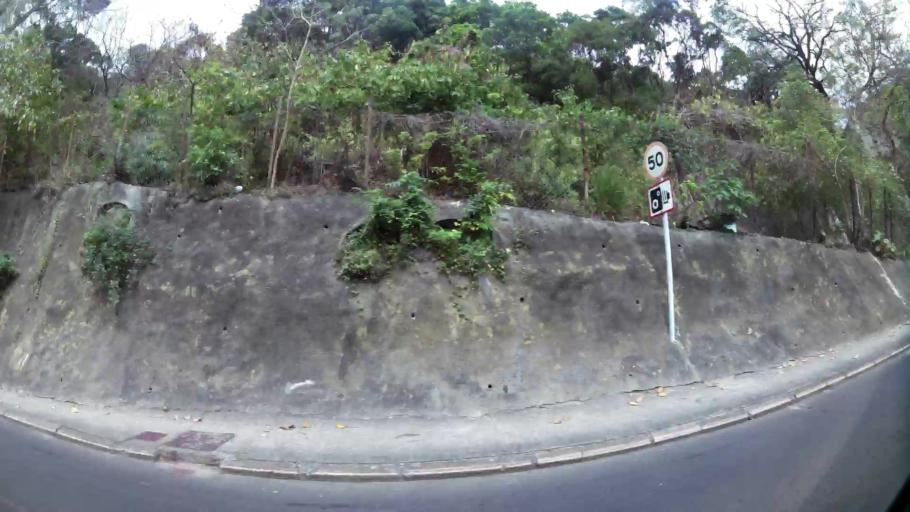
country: HK
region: Sham Shui Po
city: Sham Shui Po
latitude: 22.3361
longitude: 114.1622
